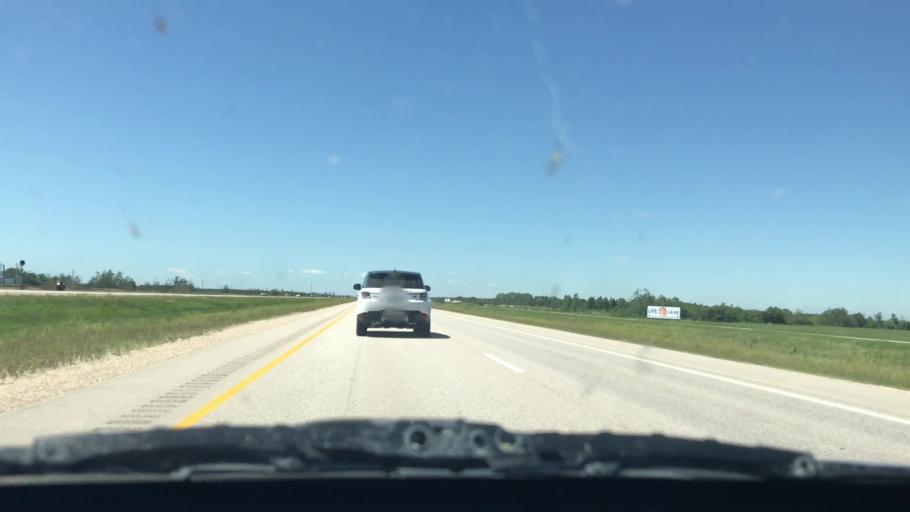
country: CA
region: Manitoba
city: Niverville
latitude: 49.8051
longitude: -96.8990
